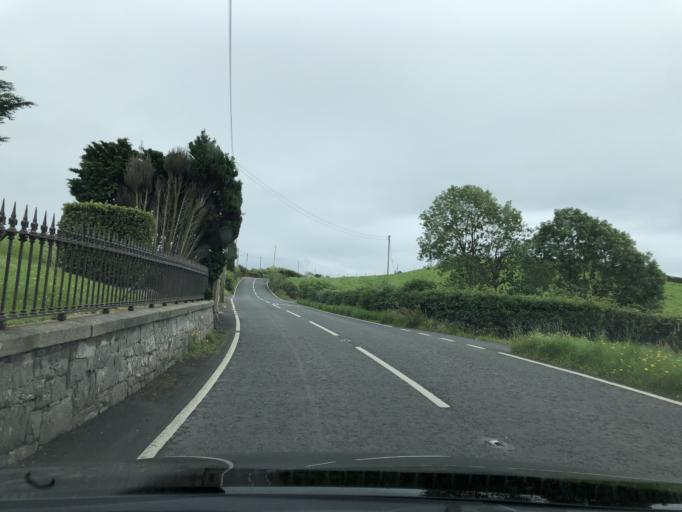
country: GB
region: Northern Ireland
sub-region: Down District
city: Dundrum
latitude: 54.2706
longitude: -5.7879
